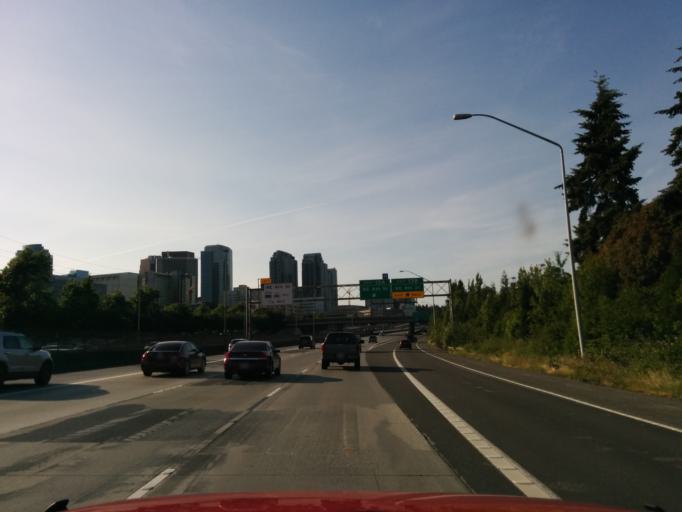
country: US
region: Washington
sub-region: King County
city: Bellevue
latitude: 47.6076
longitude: -122.1875
